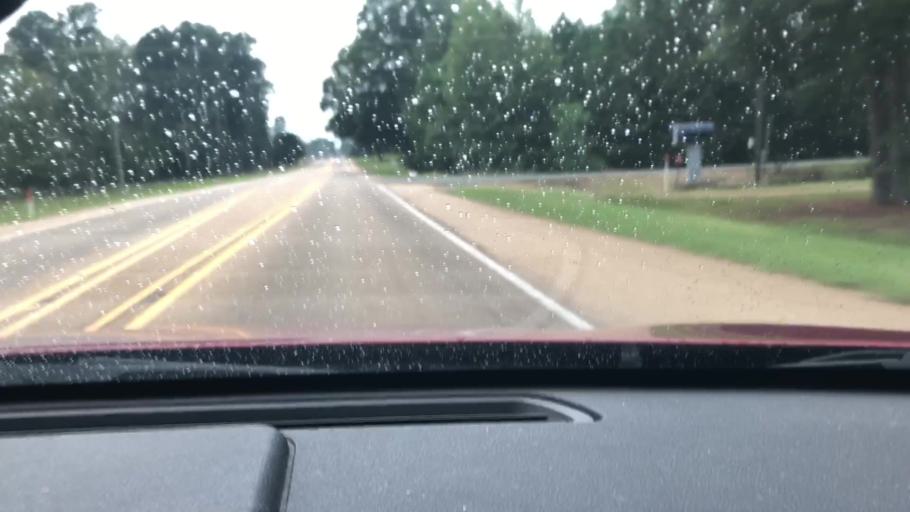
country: US
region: Arkansas
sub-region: Lafayette County
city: Stamps
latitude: 33.3650
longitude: -93.4792
